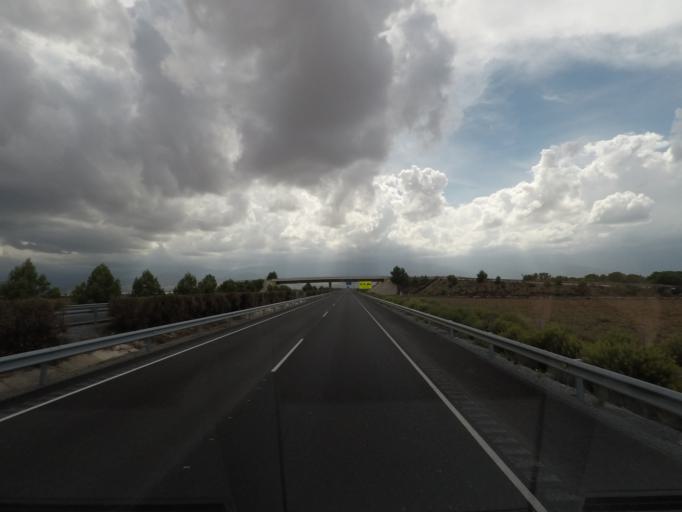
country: ES
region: Andalusia
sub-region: Provincia de Granada
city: Albunan
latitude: 37.2471
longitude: -3.0818
